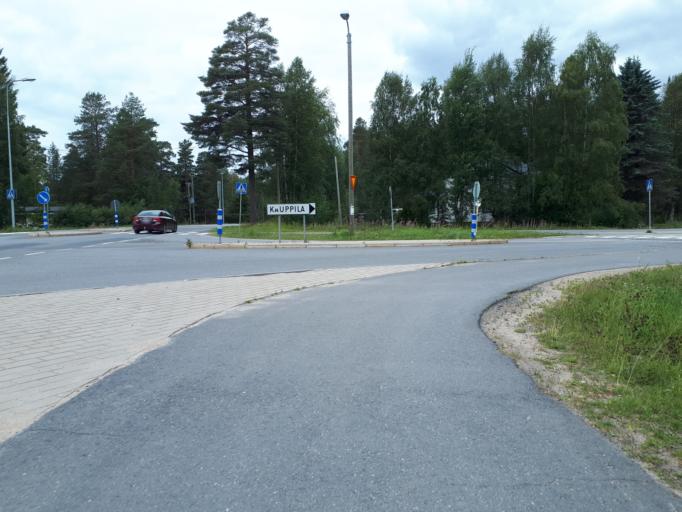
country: FI
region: Northern Ostrobothnia
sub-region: Oulunkaari
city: Ii
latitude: 65.3164
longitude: 25.3876
